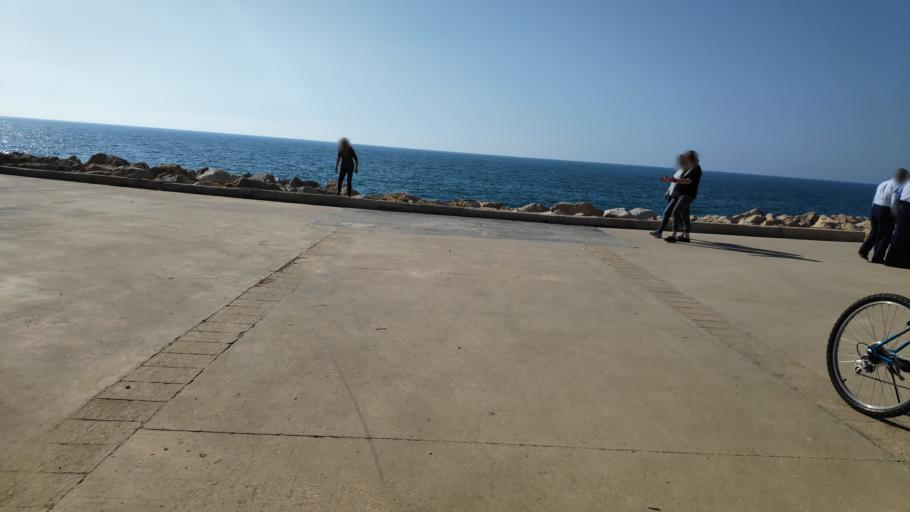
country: IL
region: Tel Aviv
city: Yafo
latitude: 32.0465
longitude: 34.7456
